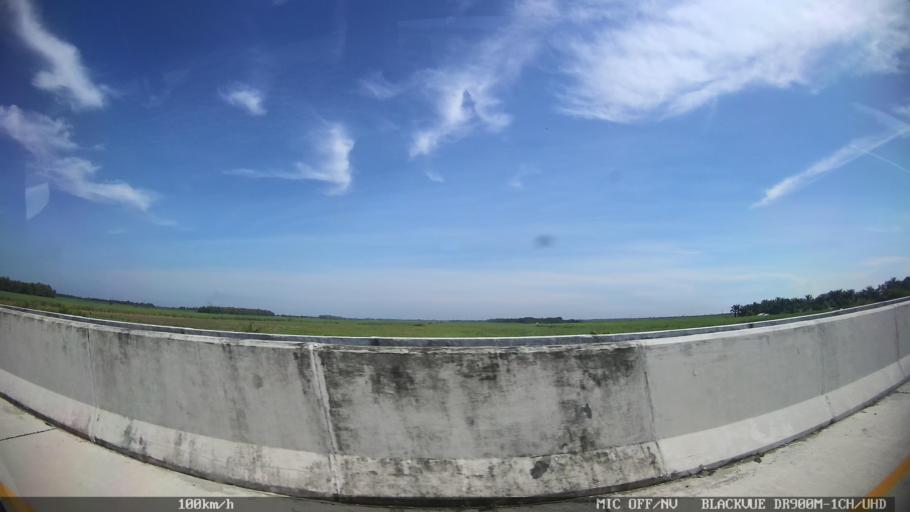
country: ID
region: North Sumatra
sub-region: Kabupaten Langkat
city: Stabat
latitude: 3.7135
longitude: 98.5228
